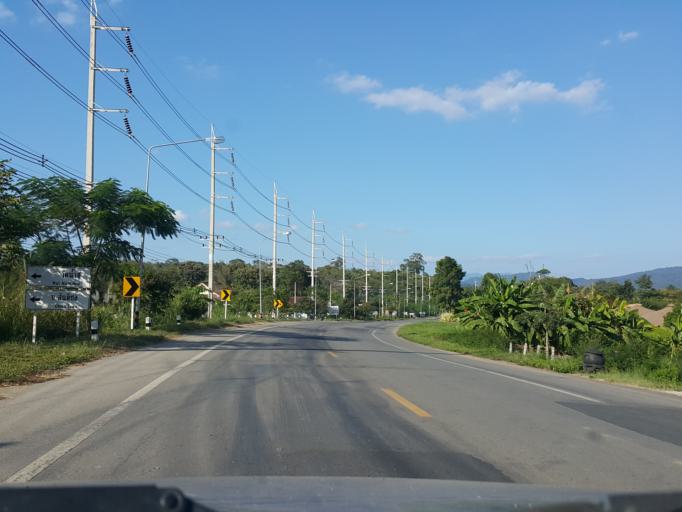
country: TH
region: Chiang Mai
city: Pai
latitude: 19.3646
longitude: 98.4255
